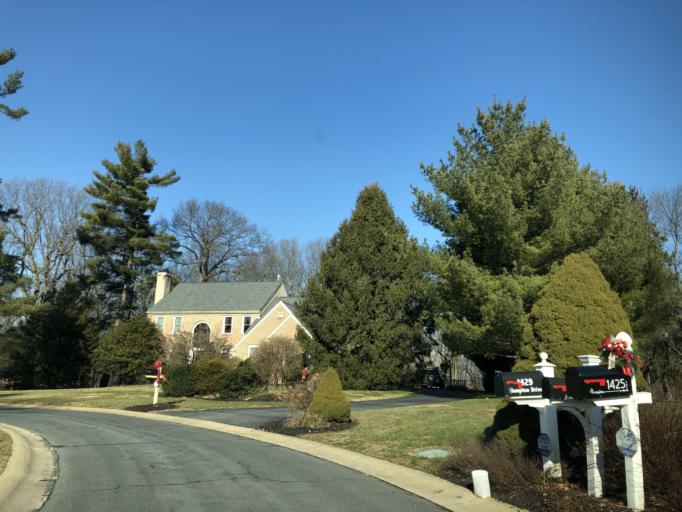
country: US
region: Pennsylvania
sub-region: Chester County
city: Downingtown
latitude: 39.9908
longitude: -75.6988
